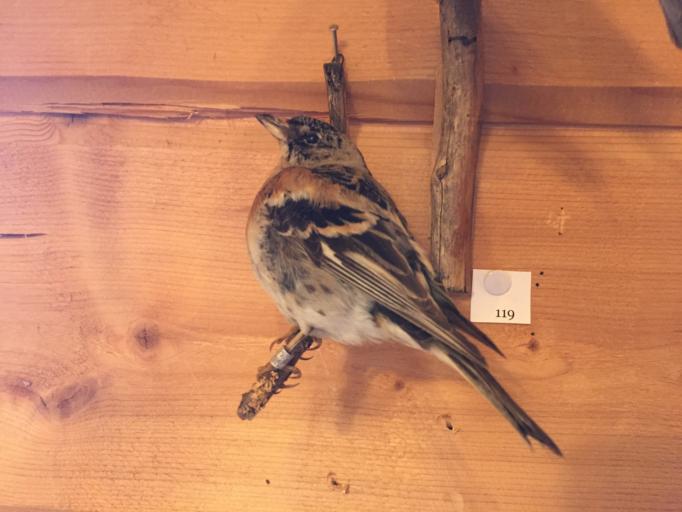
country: SE
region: OErebro
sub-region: Orebro Kommun
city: Garphyttan
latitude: 59.3360
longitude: 15.0624
